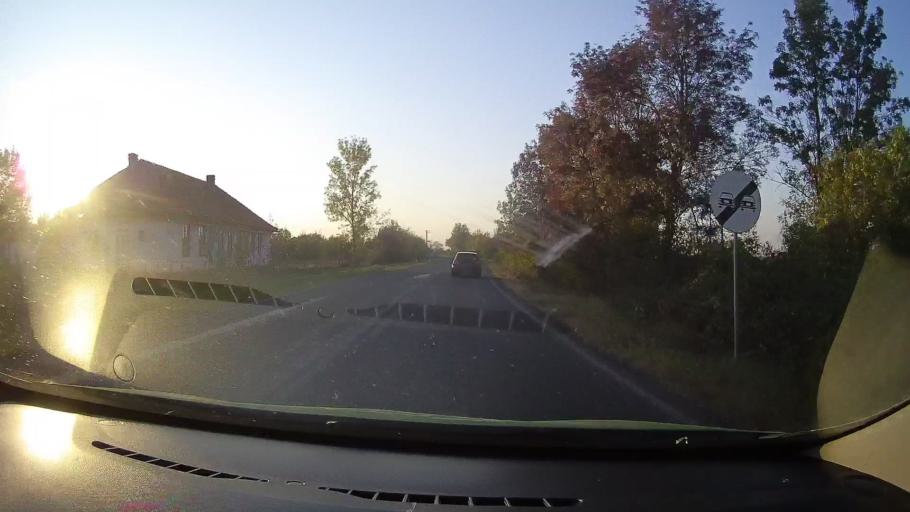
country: RO
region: Arad
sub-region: Comuna Bocsig
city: Bocsig
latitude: 46.4166
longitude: 21.9840
